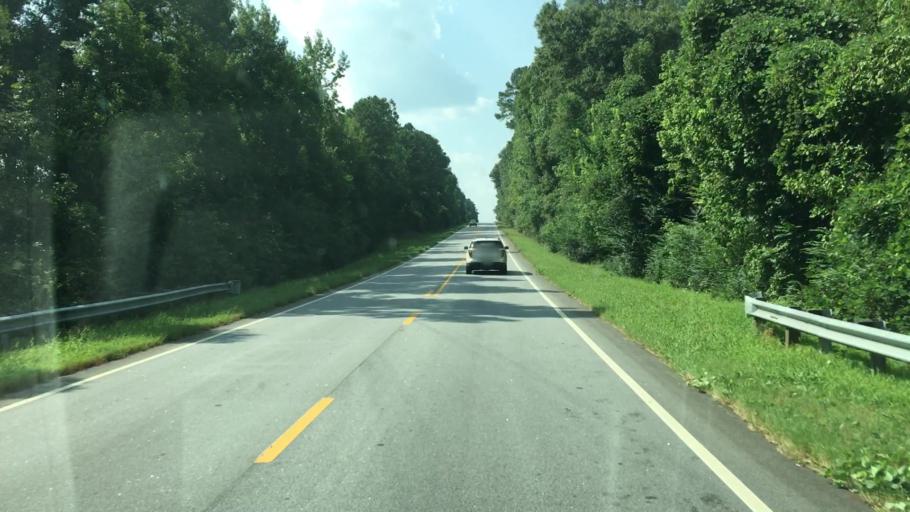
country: US
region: Georgia
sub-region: Jasper County
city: Monticello
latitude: 33.3217
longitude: -83.6988
